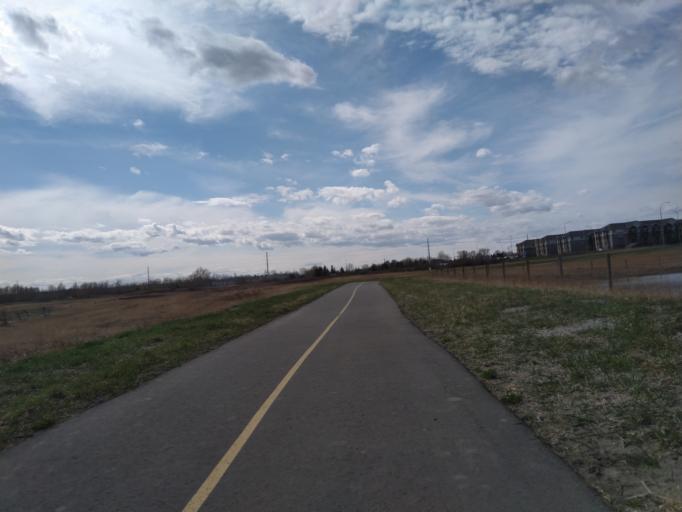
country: CA
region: Alberta
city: Chestermere
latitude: 51.0367
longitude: -113.9285
